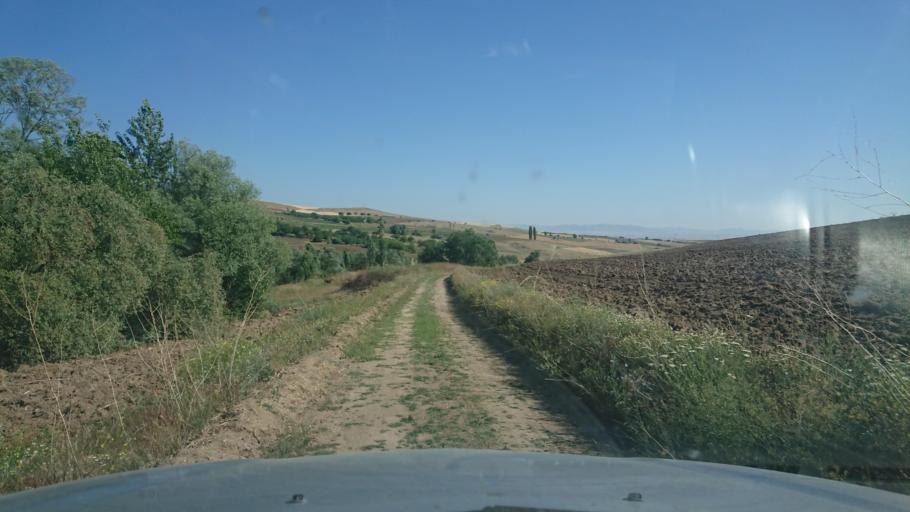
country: TR
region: Aksaray
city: Agacoren
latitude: 38.8408
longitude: 33.9257
